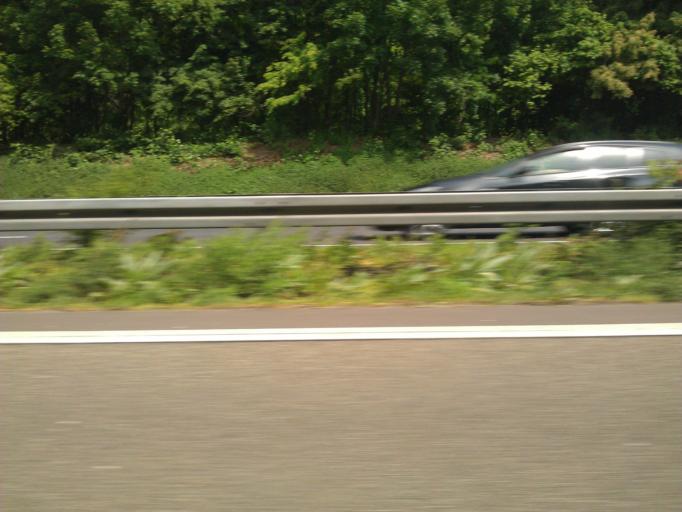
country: DE
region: North Rhine-Westphalia
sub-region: Regierungsbezirk Koln
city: Hurth
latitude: 50.9047
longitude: 6.8955
